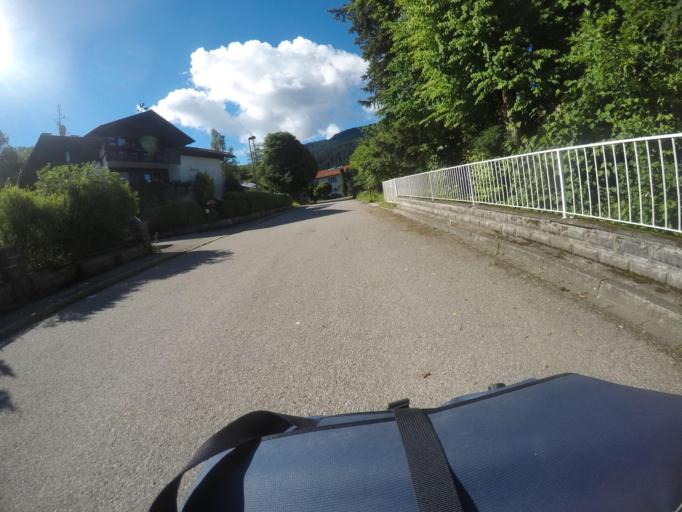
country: DE
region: Bavaria
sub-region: Swabia
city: Nesselwang
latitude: 47.6218
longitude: 10.5066
